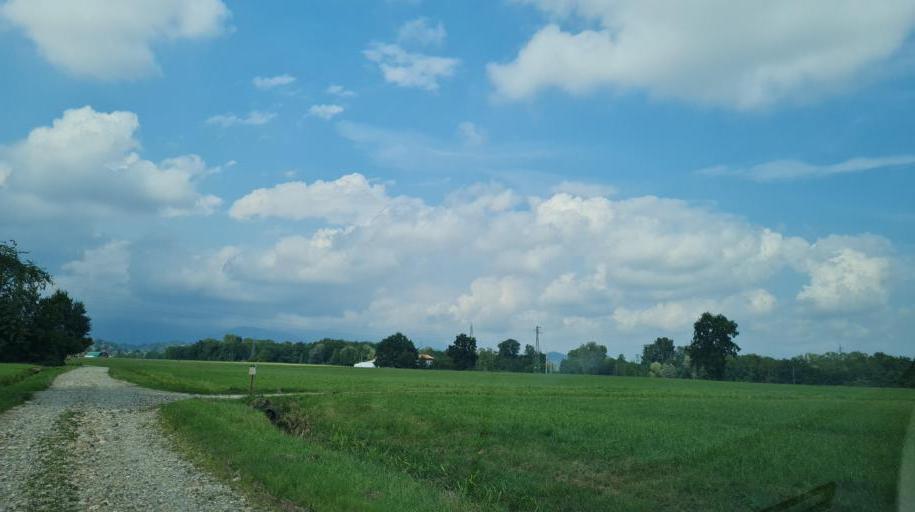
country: IT
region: Piedmont
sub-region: Provincia di Biella
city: Occhieppo Inferiore
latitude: 45.5330
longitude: 8.0320
